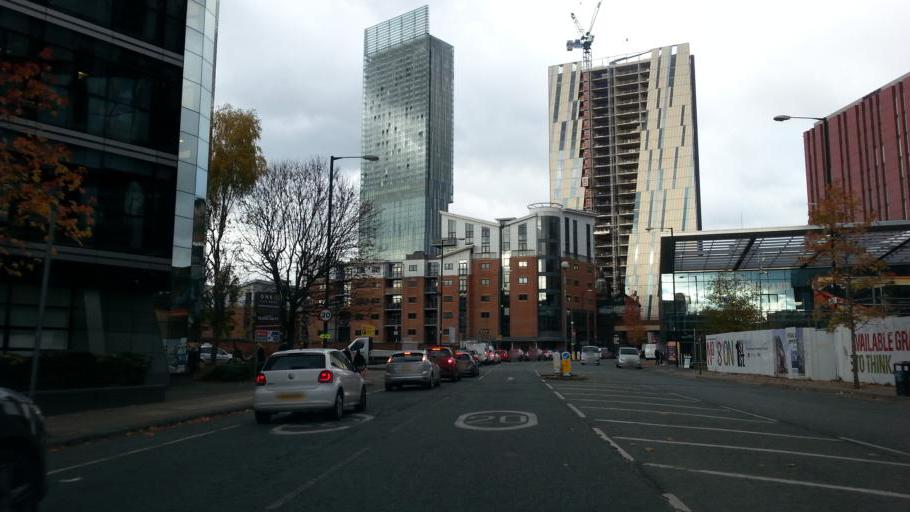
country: GB
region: England
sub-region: Manchester
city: Hulme
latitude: 53.4725
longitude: -2.2479
